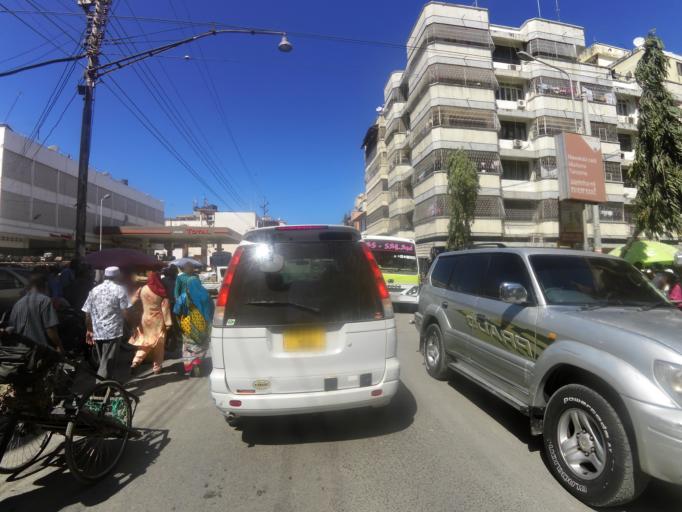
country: TZ
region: Dar es Salaam
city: Dar es Salaam
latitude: -6.8230
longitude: 39.2755
